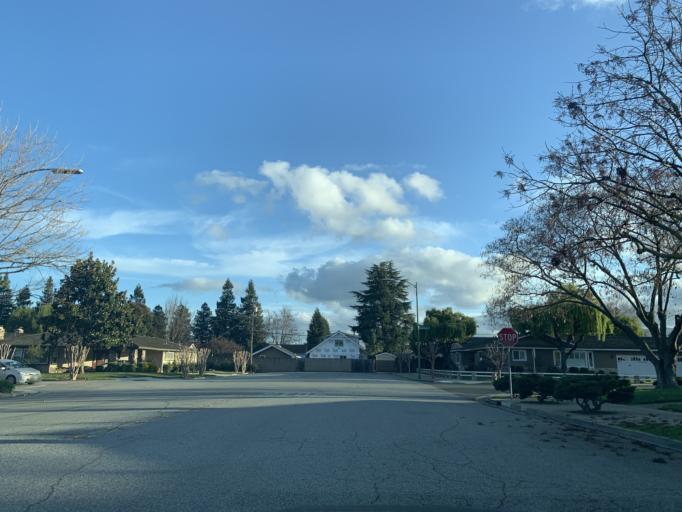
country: US
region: California
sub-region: Santa Clara County
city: Buena Vista
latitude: 37.2923
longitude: -121.9021
